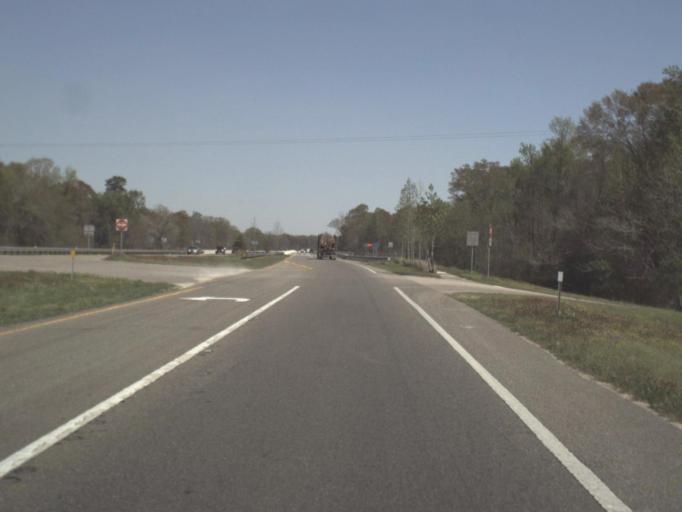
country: US
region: Florida
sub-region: Calhoun County
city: Blountstown
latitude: 30.4430
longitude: -85.0208
